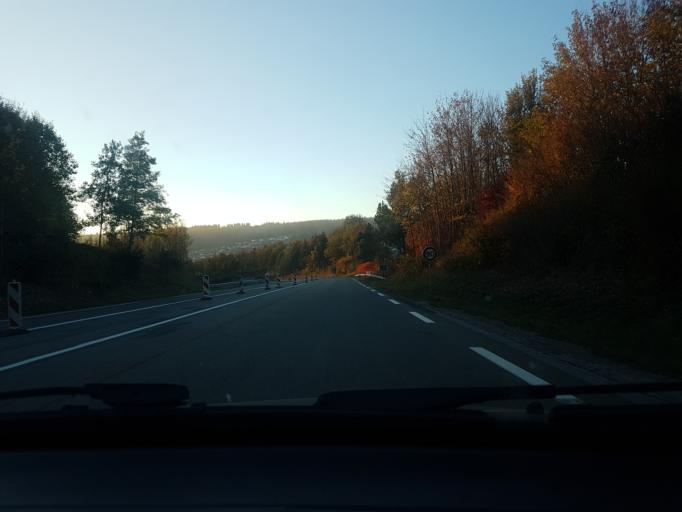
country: FR
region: Franche-Comte
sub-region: Departement du Doubs
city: Villers-le-Lac
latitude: 47.0585
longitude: 6.6816
